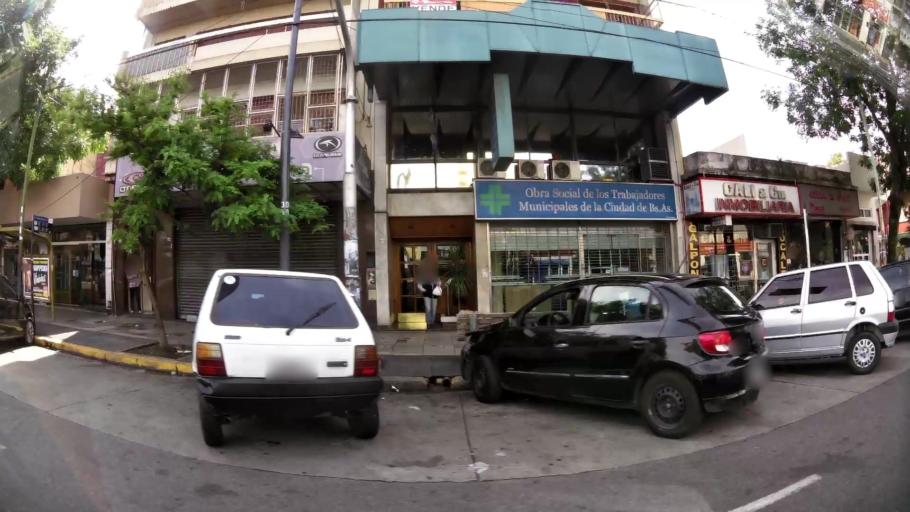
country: AR
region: Buenos Aires F.D.
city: Villa Lugano
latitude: -34.6533
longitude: -58.5043
